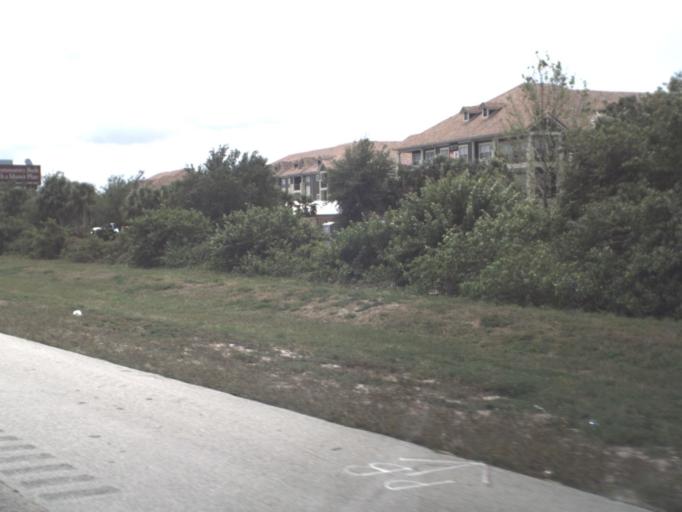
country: US
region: Florida
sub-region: Brevard County
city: Rockledge
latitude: 28.2486
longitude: -80.7240
